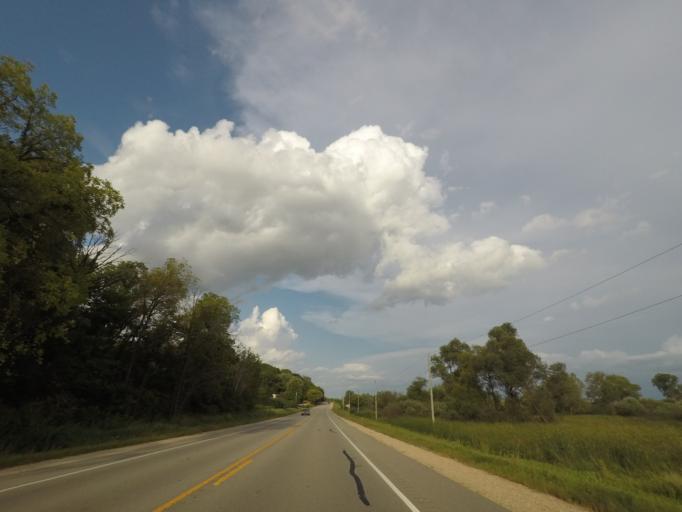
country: US
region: Wisconsin
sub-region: Dane County
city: Waunakee
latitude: 43.1885
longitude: -89.5444
